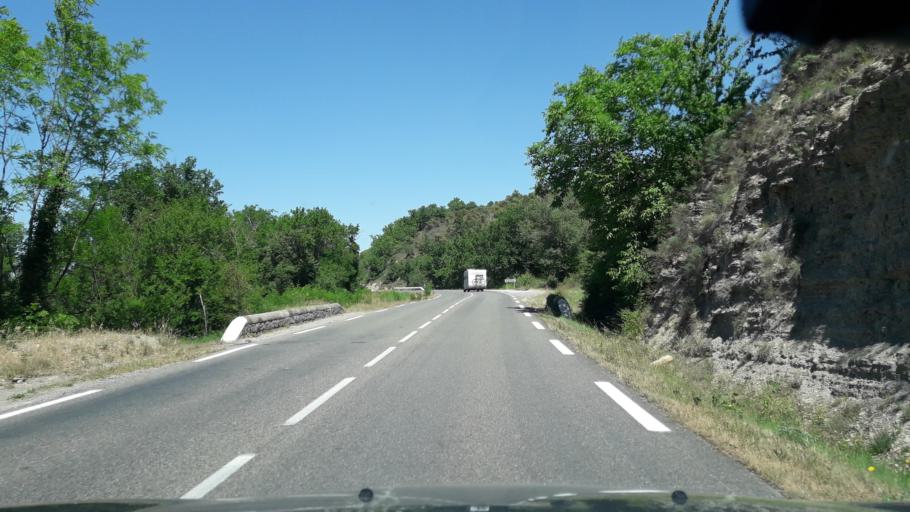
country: FR
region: Rhone-Alpes
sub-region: Departement de l'Ardeche
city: Ruoms
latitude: 44.4118
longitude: 4.3009
